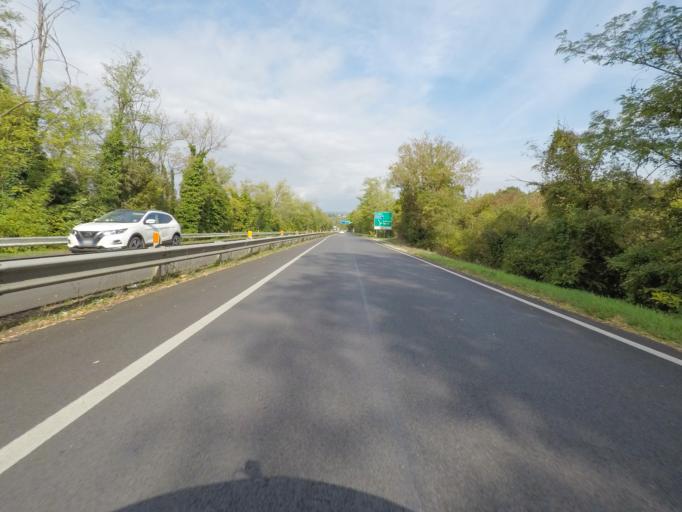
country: IT
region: Tuscany
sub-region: Provincia di Siena
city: Belverde
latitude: 43.3517
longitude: 11.3059
